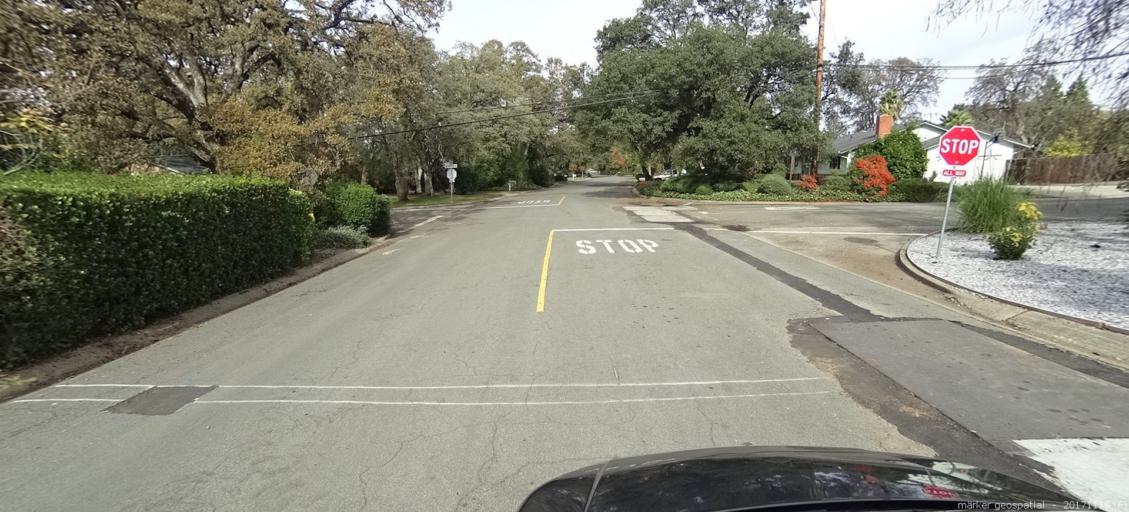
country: US
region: California
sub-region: Shasta County
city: Anderson
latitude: 40.4909
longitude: -122.3094
